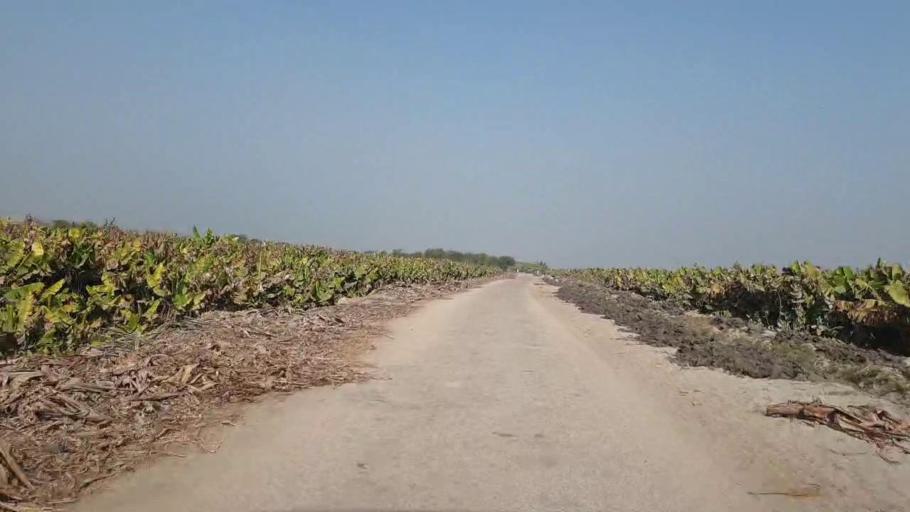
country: PK
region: Sindh
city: Bhit Shah
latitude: 25.7758
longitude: 68.4939
